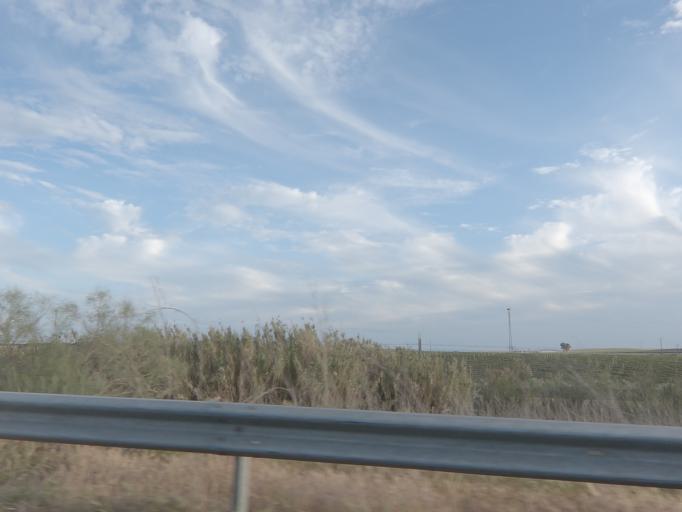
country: ES
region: Extremadura
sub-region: Provincia de Badajoz
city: Lobon
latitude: 38.8395
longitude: -6.6551
